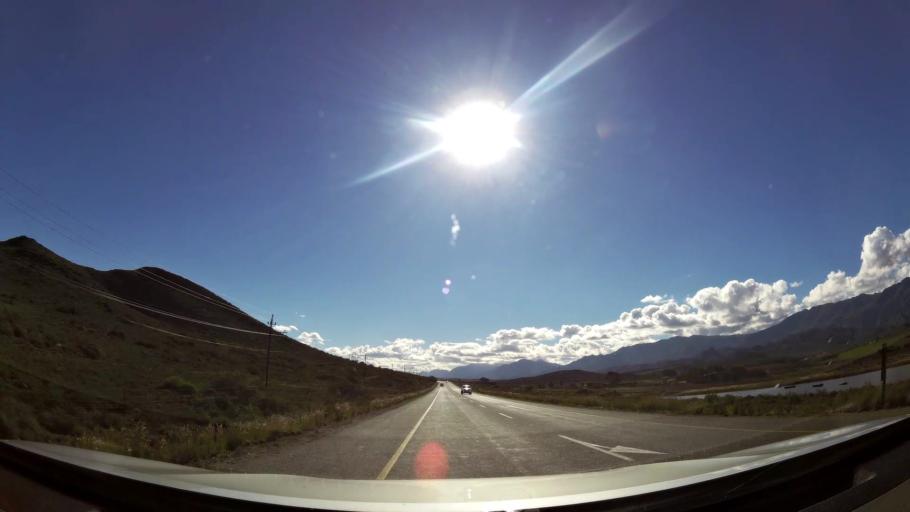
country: ZA
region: Western Cape
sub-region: Cape Winelands District Municipality
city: Ashton
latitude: -33.7827
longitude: 19.7685
